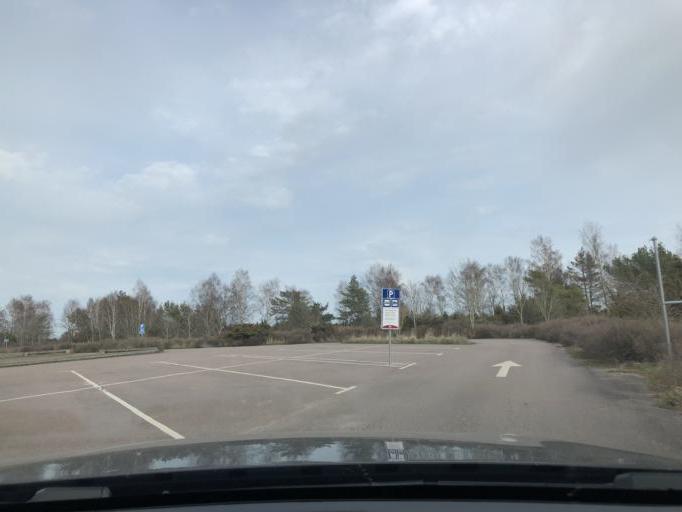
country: SE
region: Kalmar
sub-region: Morbylanga Kommun
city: Moerbylanga
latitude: 56.2915
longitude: 16.4831
